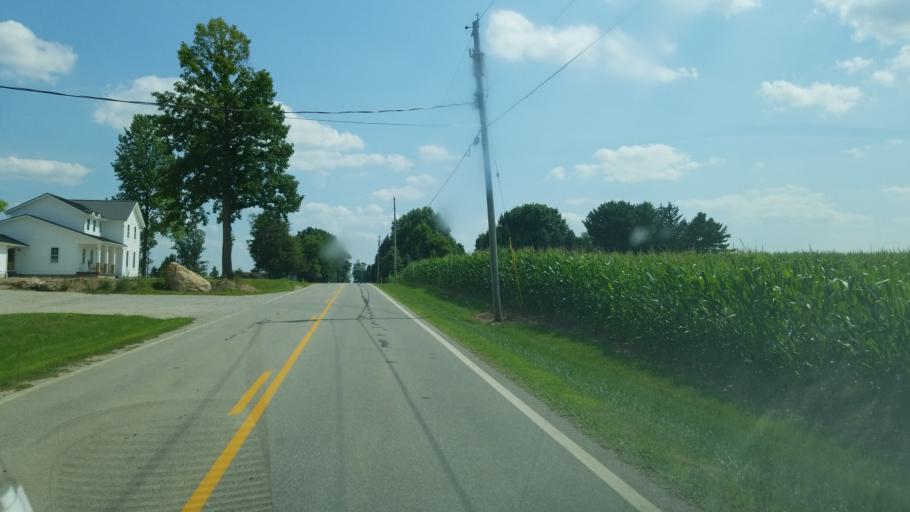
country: US
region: Ohio
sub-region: Huron County
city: Plymouth
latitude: 41.0967
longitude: -82.6114
